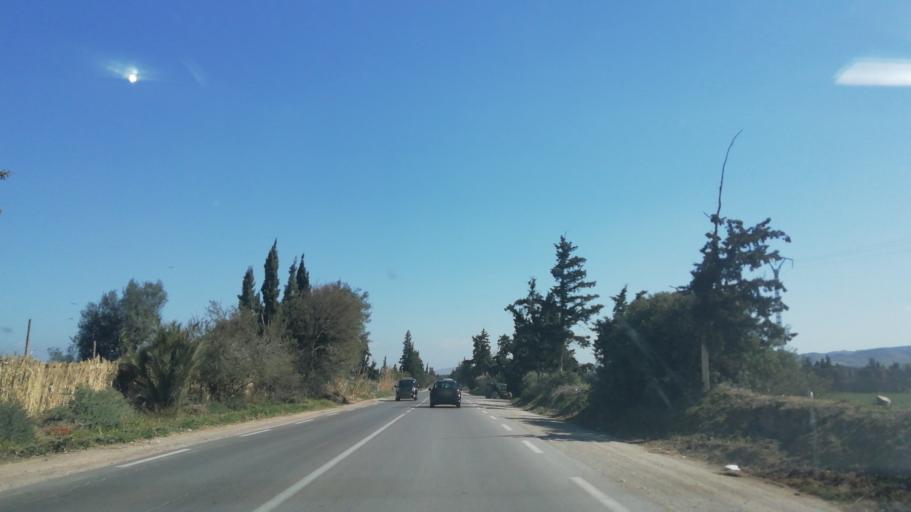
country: DZ
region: Mascara
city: Sig
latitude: 35.5716
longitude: -0.0297
